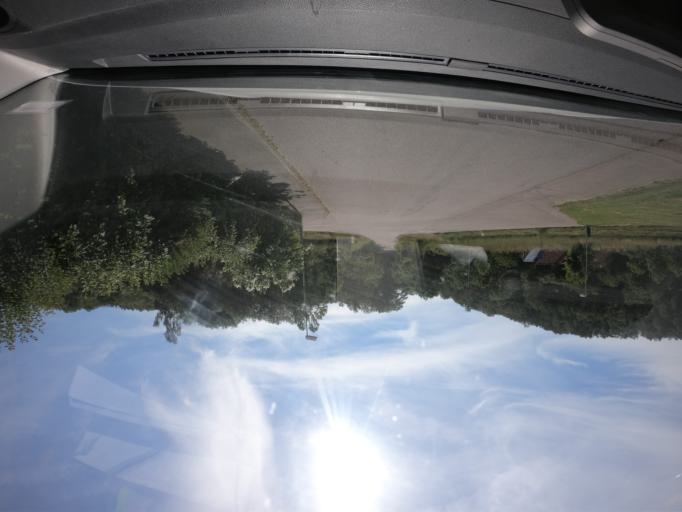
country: SE
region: Skane
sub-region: Bastads Kommun
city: Bastad
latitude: 56.4188
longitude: 12.8558
